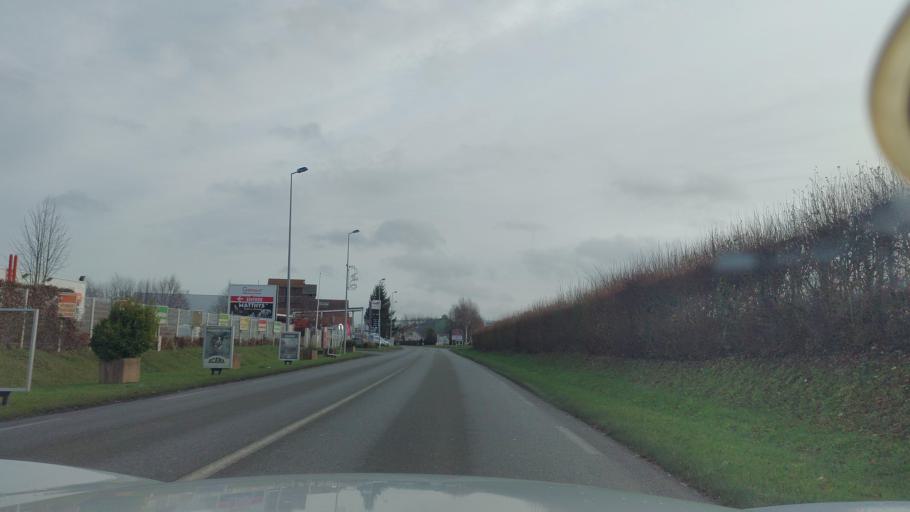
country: FR
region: Picardie
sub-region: Departement de la Somme
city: Oisemont
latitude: 49.9606
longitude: 1.7644
